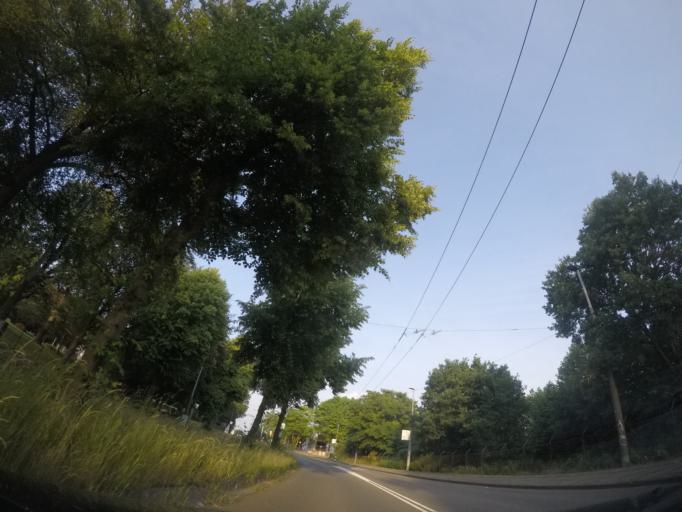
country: NL
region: Gelderland
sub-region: Gemeente Arnhem
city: Hoogkamp
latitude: 51.9837
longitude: 5.8681
